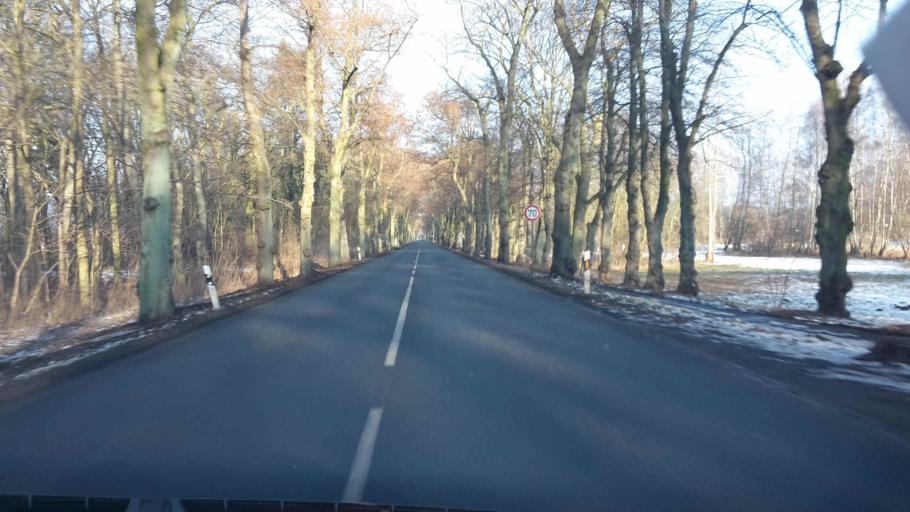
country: DE
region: Brandenburg
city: Perleberg
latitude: 53.0625
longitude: 11.8420
